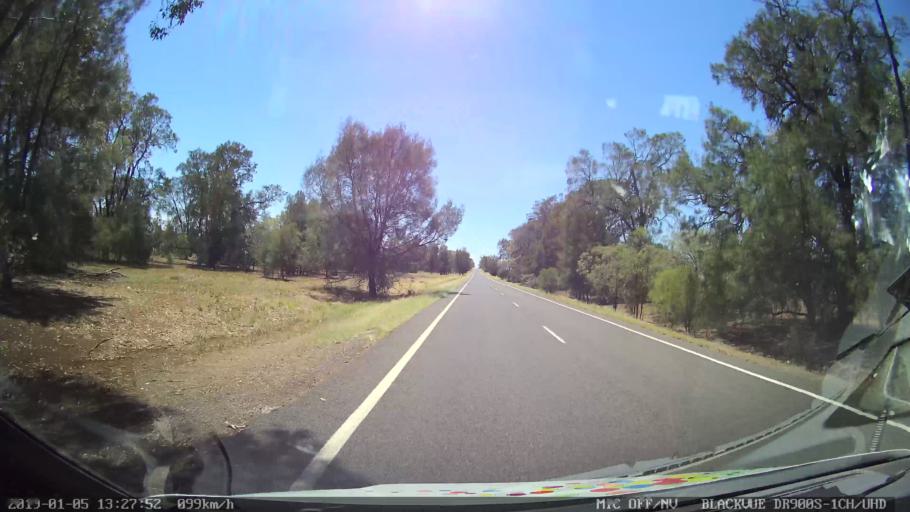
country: AU
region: New South Wales
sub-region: Gunnedah
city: Gunnedah
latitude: -31.0409
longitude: 150.0352
